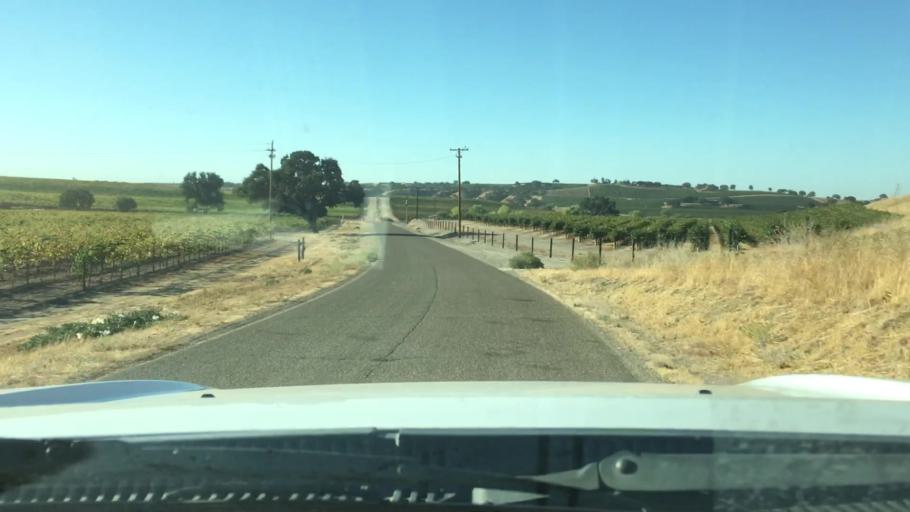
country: US
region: California
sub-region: San Luis Obispo County
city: San Miguel
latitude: 35.7210
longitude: -120.6316
